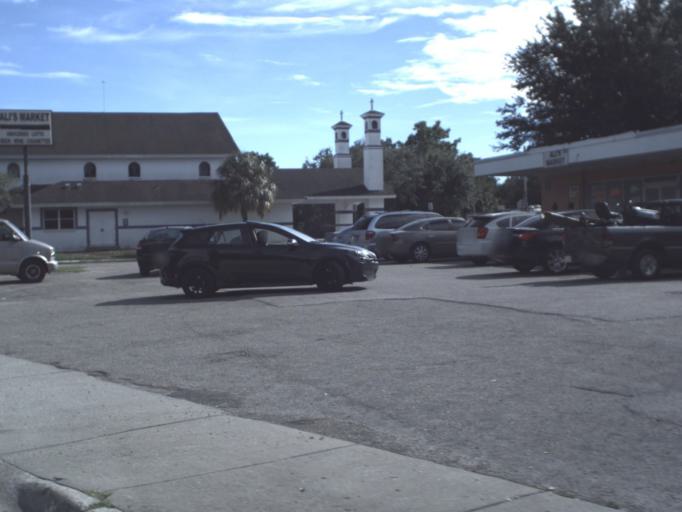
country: US
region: Florida
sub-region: Manatee County
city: Memphis
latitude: 27.5345
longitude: -82.5617
